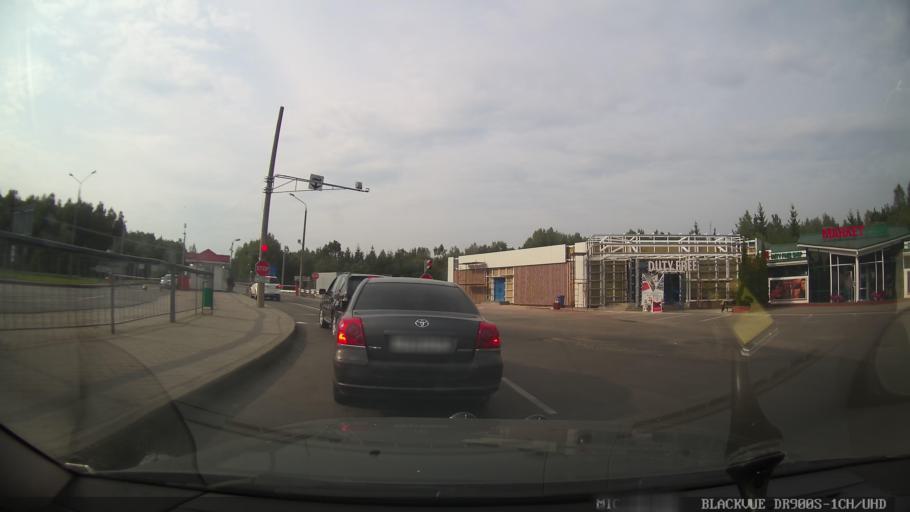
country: BY
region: Grodnenskaya
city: Astravyets
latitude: 54.5441
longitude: 25.7008
